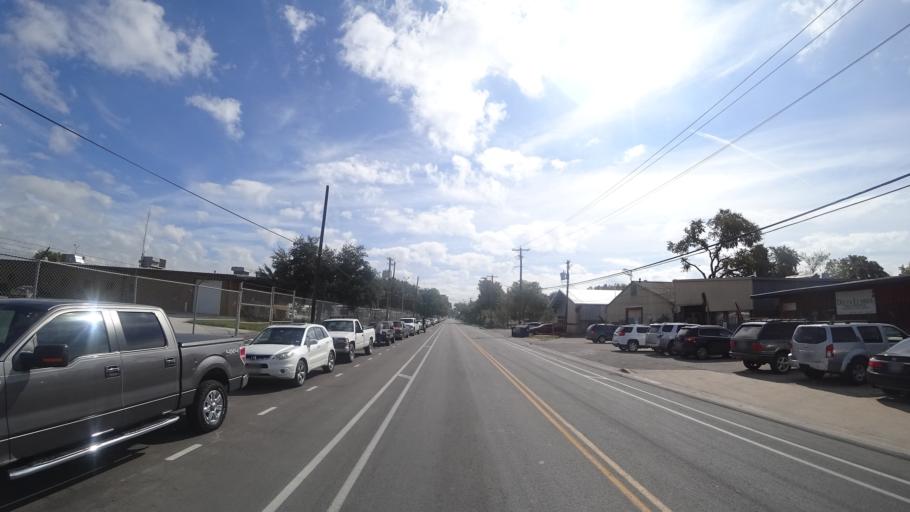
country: US
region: Texas
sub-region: Travis County
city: Austin
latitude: 30.2537
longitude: -97.7029
